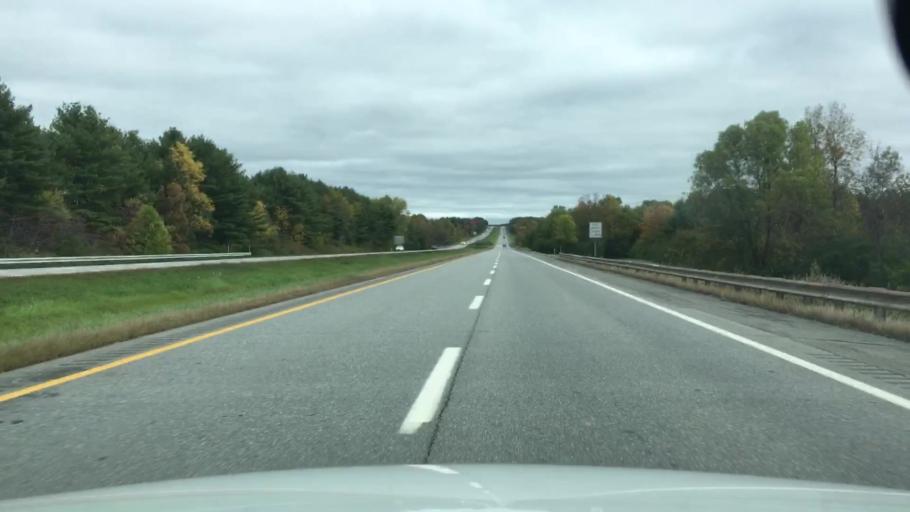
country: US
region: Maine
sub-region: Penobscot County
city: Newport
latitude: 44.8282
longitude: -69.2800
